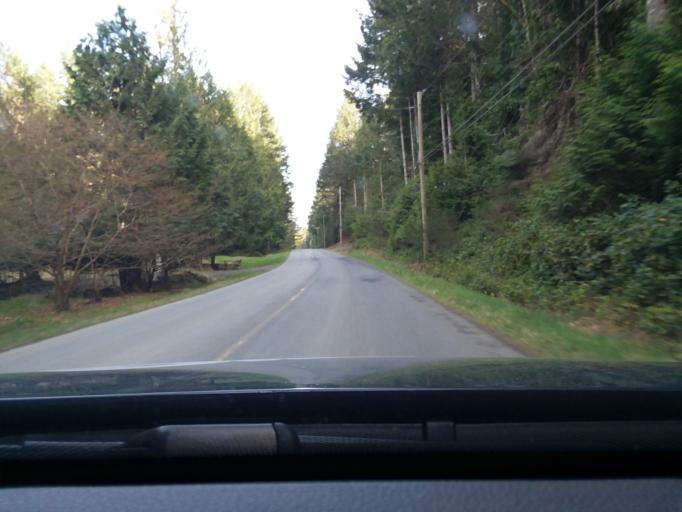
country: CA
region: British Columbia
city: North Saanich
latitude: 48.7508
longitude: -123.2633
